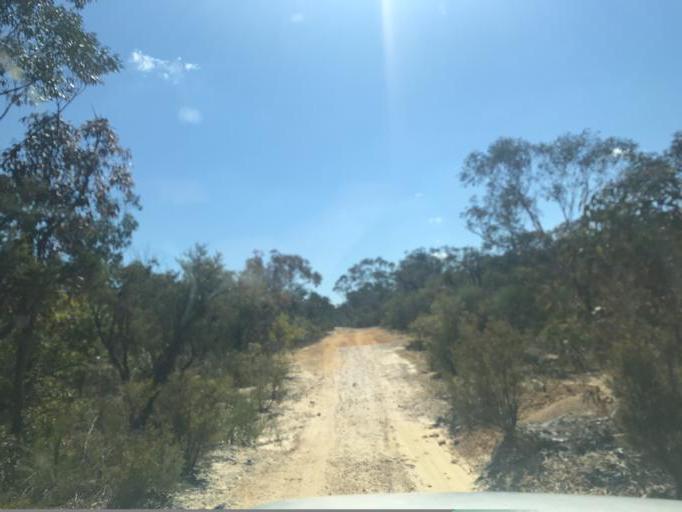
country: AU
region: New South Wales
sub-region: Wyong Shire
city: Little Jilliby
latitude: -33.1583
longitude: 151.0989
